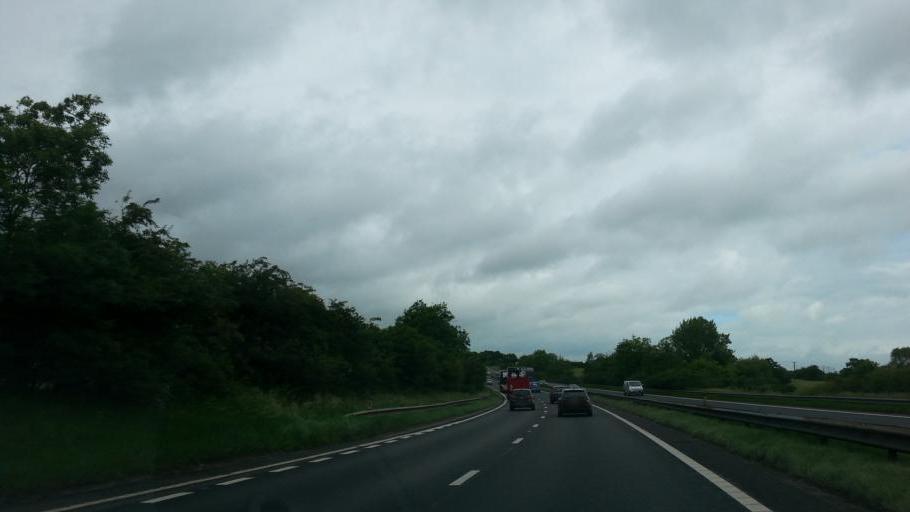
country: GB
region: England
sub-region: City and Borough of Wakefield
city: Darrington
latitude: 53.6714
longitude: -1.2615
